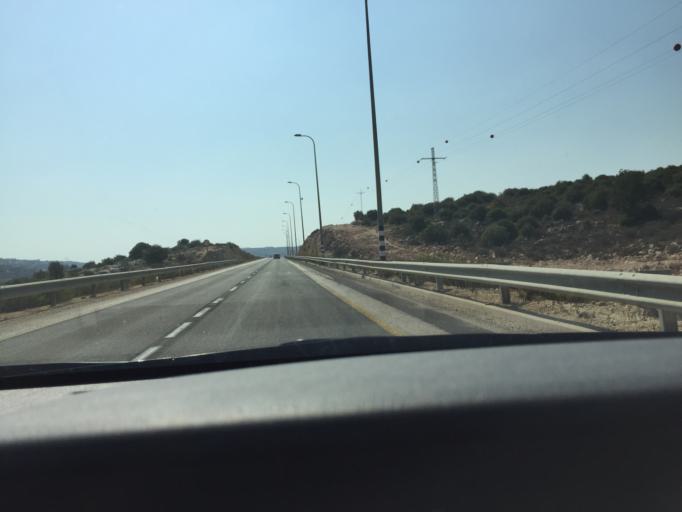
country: PS
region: West Bank
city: Bruqin
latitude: 32.0802
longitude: 35.1004
